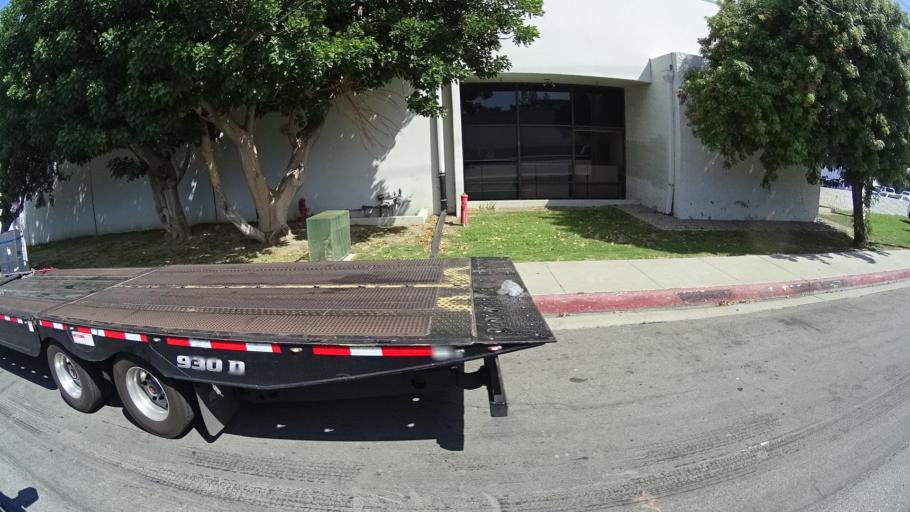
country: US
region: California
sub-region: Los Angeles County
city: South San Jose Hills
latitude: 33.9977
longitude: -117.8907
